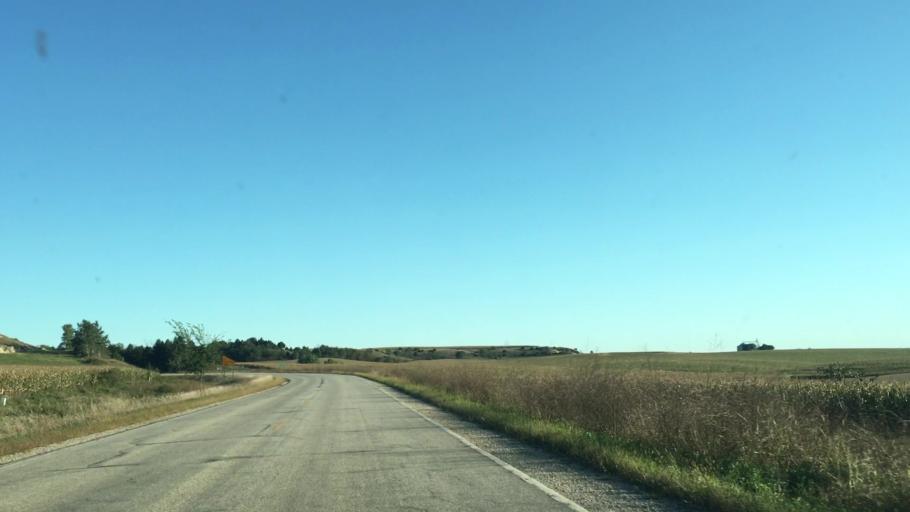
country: US
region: Minnesota
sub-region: Fillmore County
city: Chatfield
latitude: 43.8490
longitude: -92.1065
